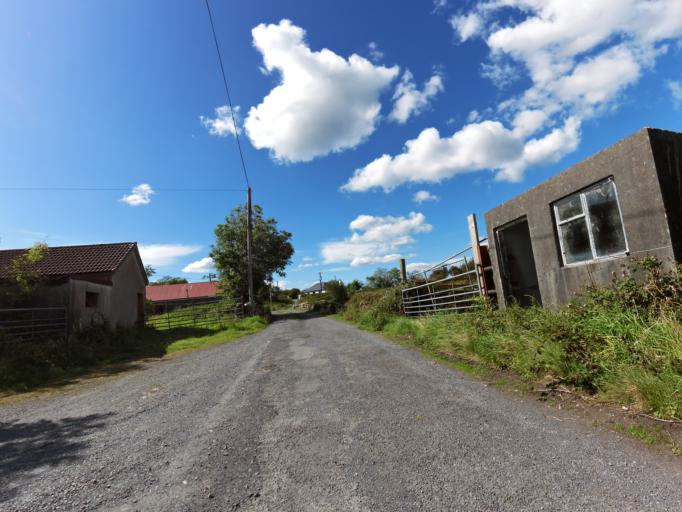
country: IE
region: Connaught
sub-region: County Galway
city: Gaillimh
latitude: 53.2856
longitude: -9.0909
